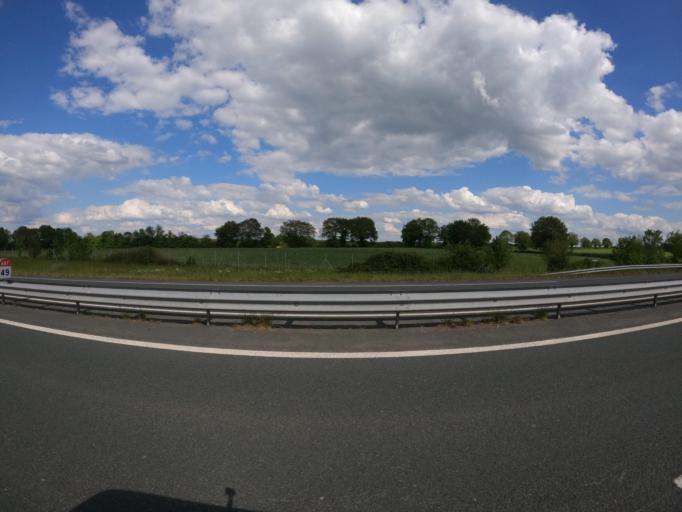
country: FR
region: Pays de la Loire
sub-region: Departement de Maine-et-Loire
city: Mazieres-en-Mauges
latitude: 47.0718
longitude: -0.8263
